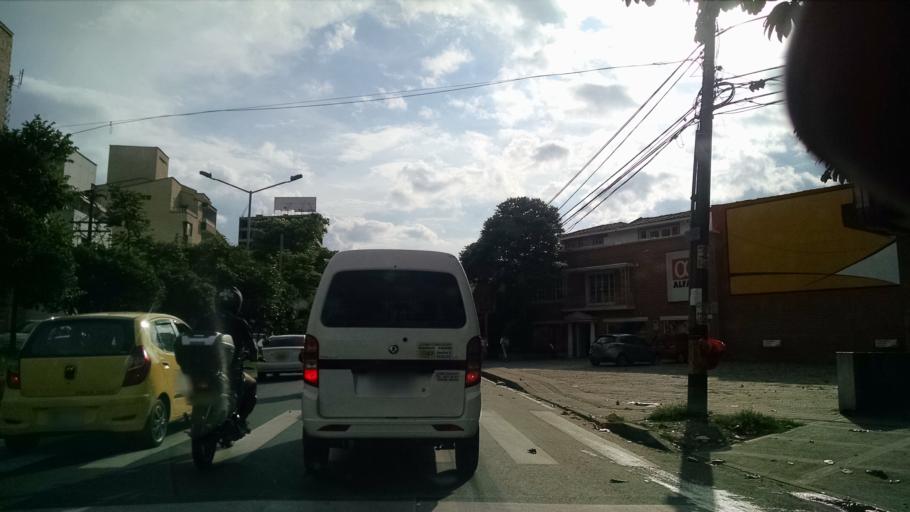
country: CO
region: Antioquia
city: Medellin
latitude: 6.2465
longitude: -75.5828
